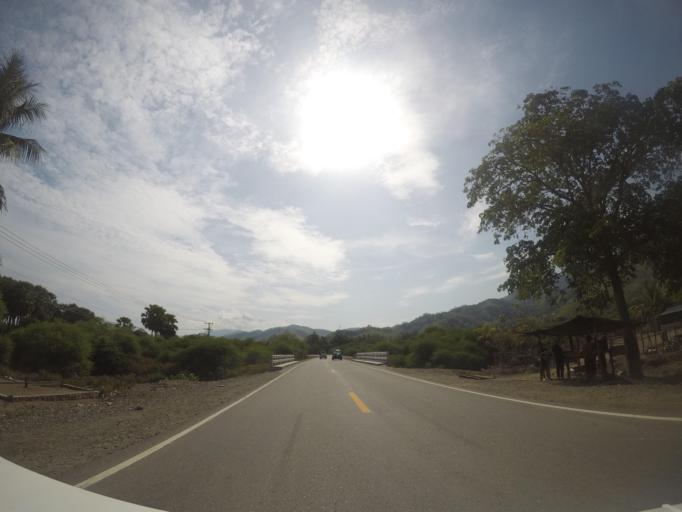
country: ID
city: Metinaro
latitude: -8.5313
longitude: 125.7474
